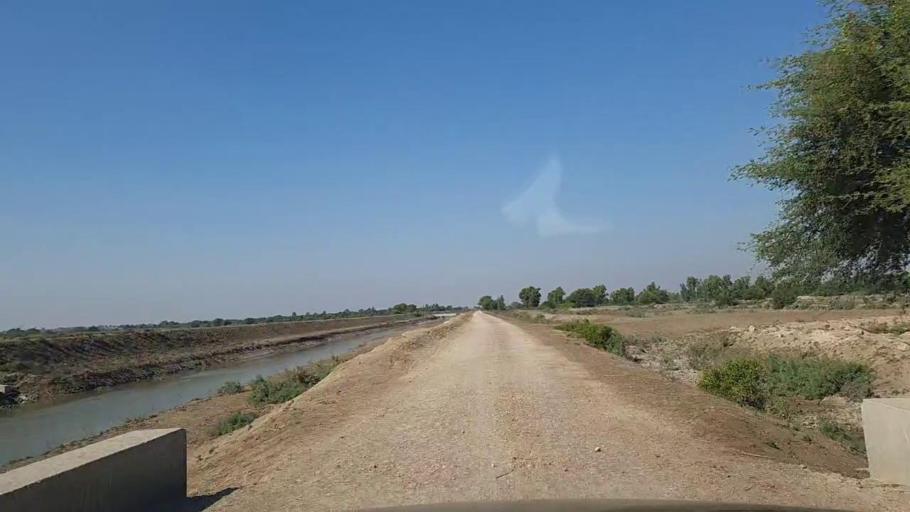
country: PK
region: Sindh
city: Mirpur Batoro
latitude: 24.7229
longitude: 68.2332
